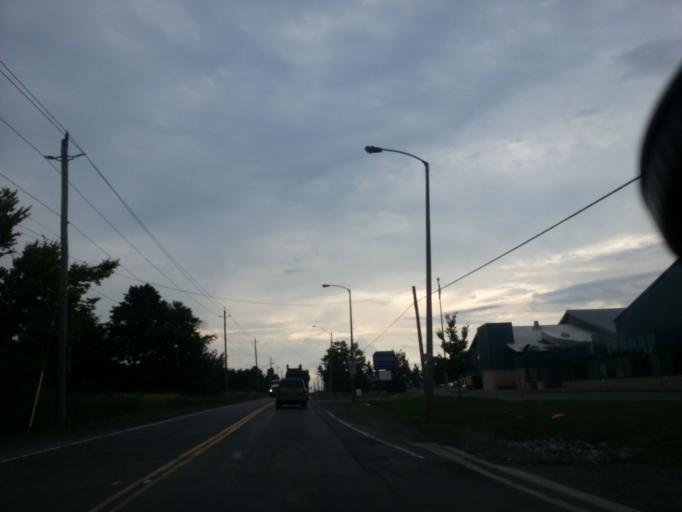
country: CA
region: Ontario
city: Ottawa
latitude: 45.3314
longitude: -75.5988
